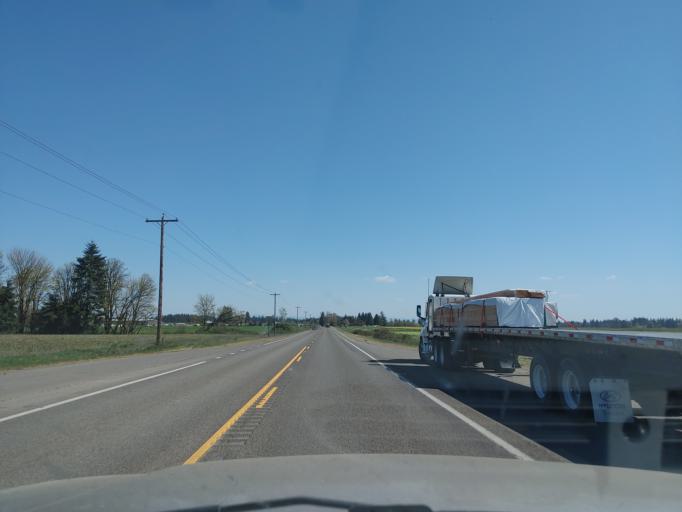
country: US
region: Oregon
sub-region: Yamhill County
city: Newberg
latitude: 45.2381
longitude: -122.9193
